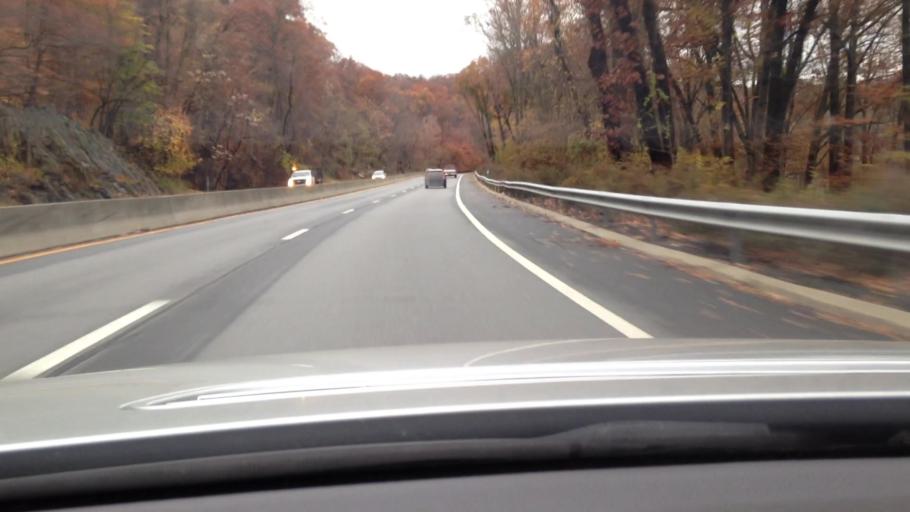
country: US
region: New York
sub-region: Westchester County
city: Elmsford
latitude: 41.0724
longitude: -73.8330
